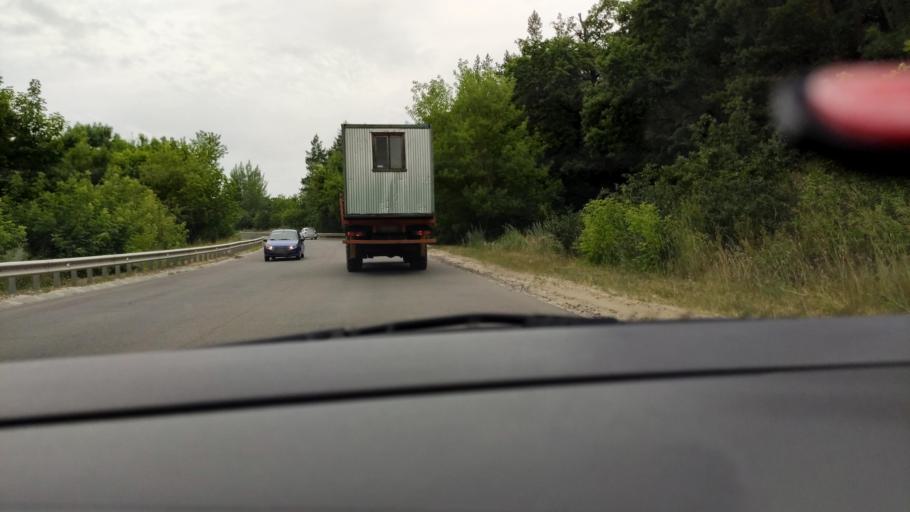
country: RU
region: Voronezj
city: Ramon'
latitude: 51.9041
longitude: 39.3394
